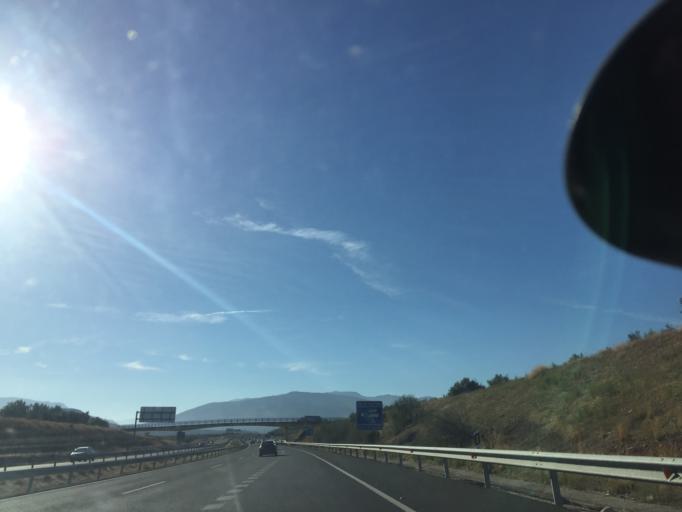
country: ES
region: Andalusia
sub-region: Provincia de Jaen
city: Jaen
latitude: 37.8094
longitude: -3.7638
